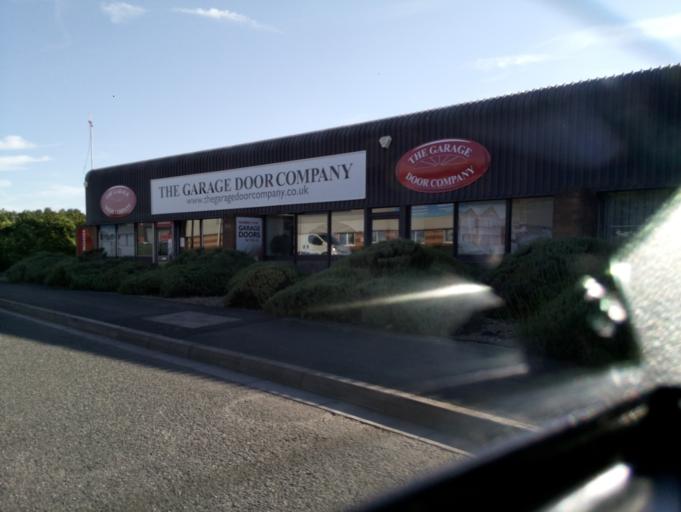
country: GB
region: England
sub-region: Bristol
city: Bristol
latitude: 51.4485
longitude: -2.5702
